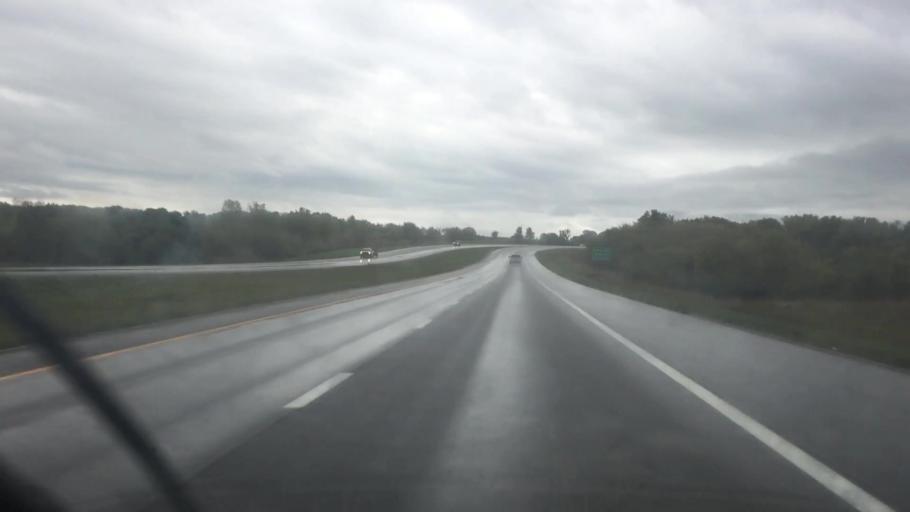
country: US
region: Kansas
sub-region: Johnson County
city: Spring Hill
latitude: 38.7342
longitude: -94.8376
